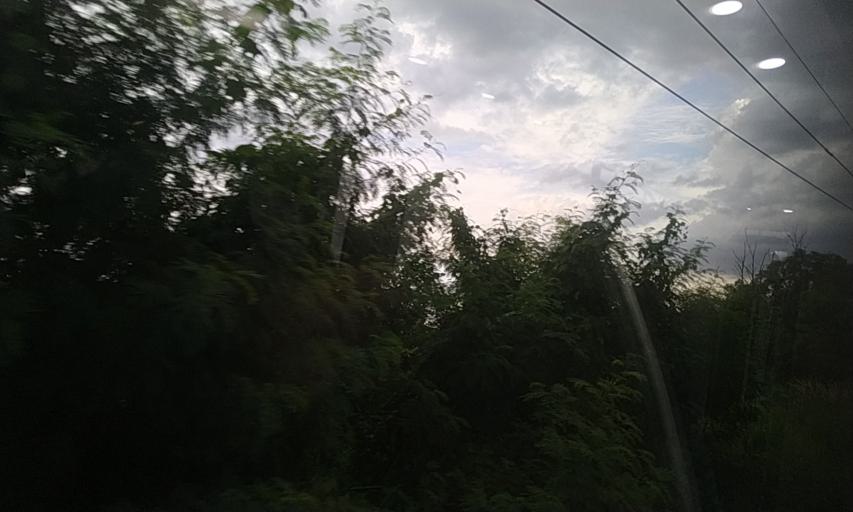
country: MY
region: Kuala Lumpur
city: Kuala Lumpur
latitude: 3.2252
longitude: 101.6727
